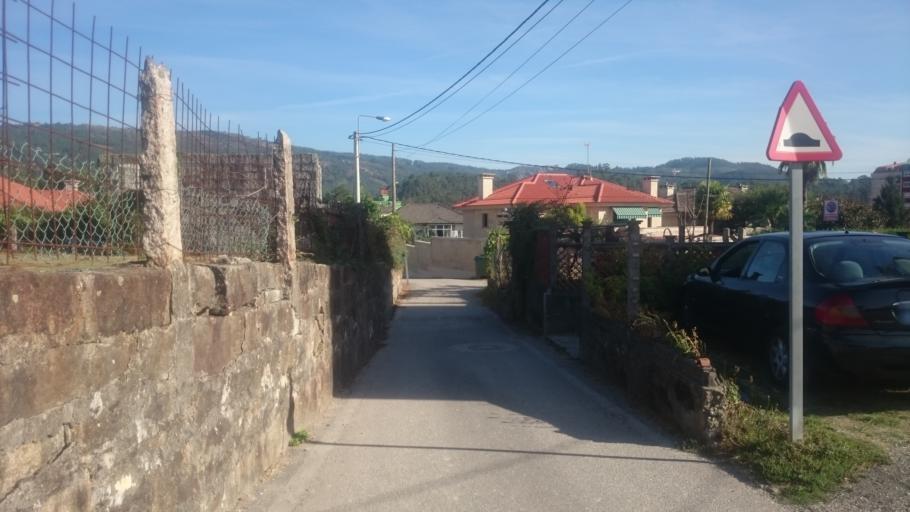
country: ES
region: Galicia
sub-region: Provincia de Pontevedra
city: Porrino
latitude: 42.1623
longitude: -8.6156
